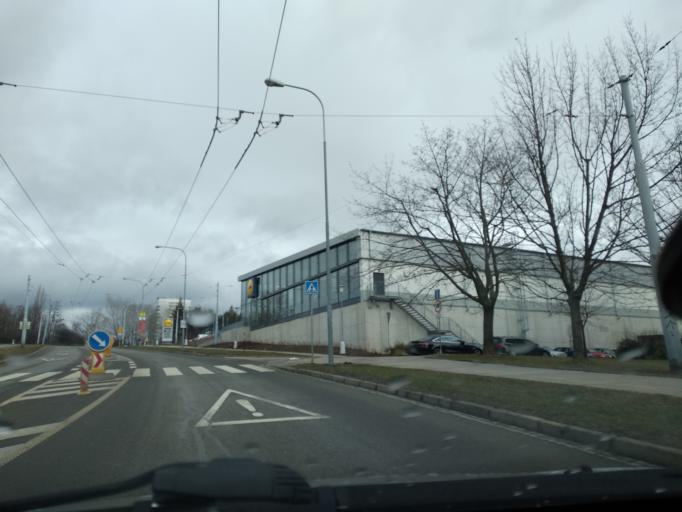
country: CZ
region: South Moravian
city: Moravany
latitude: 49.1707
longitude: 16.5691
